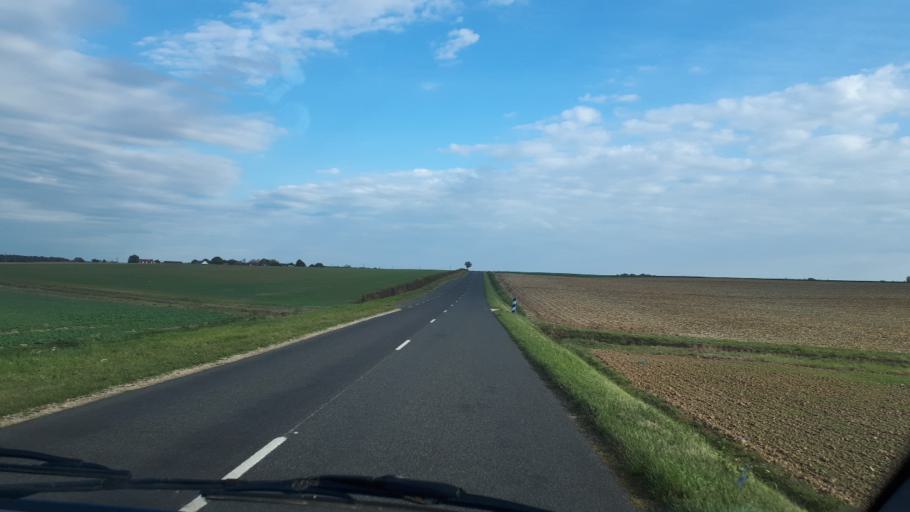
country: FR
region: Centre
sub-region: Departement du Loir-et-Cher
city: Mondoubleau
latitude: 47.9094
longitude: 0.9307
